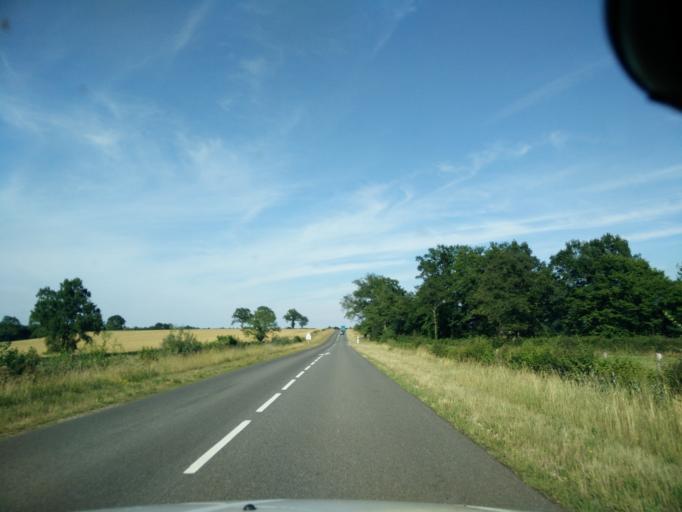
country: FR
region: Auvergne
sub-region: Departement de l'Allier
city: Souvigny
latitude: 46.5219
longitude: 3.1398
